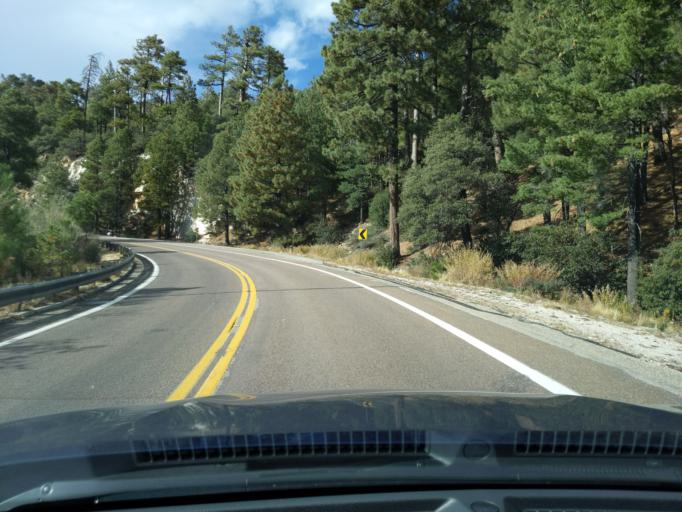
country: US
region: Arizona
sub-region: Pima County
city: Tanque Verde
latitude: 32.4091
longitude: -110.7044
